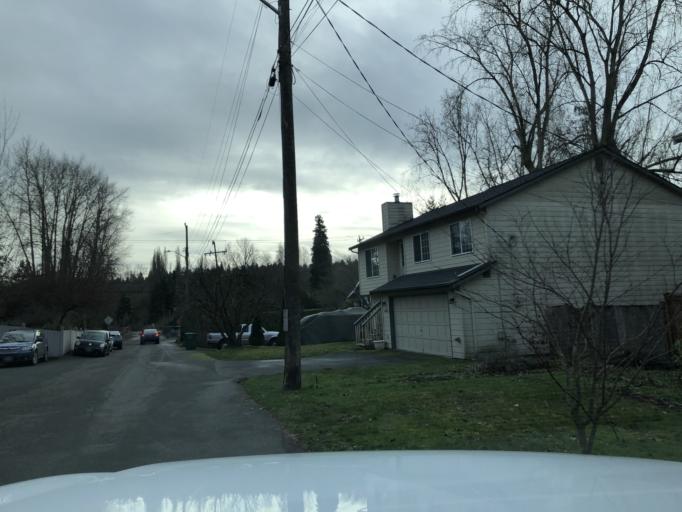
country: US
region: Washington
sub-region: King County
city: Lake Forest Park
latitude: 47.7090
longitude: -122.2894
